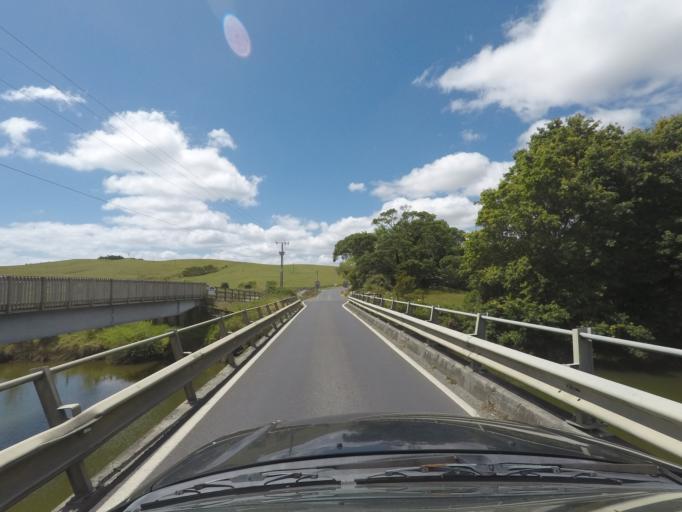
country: NZ
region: Northland
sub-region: Whangarei
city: Ruakaka
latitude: -35.9869
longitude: 174.4552
